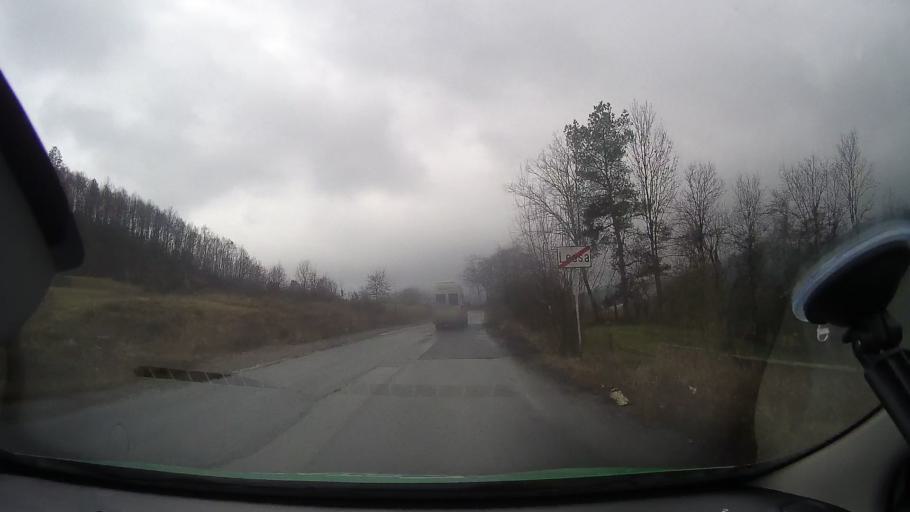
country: RO
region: Arad
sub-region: Comuna Halmagiu
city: Halmagiu
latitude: 46.2878
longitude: 22.5473
